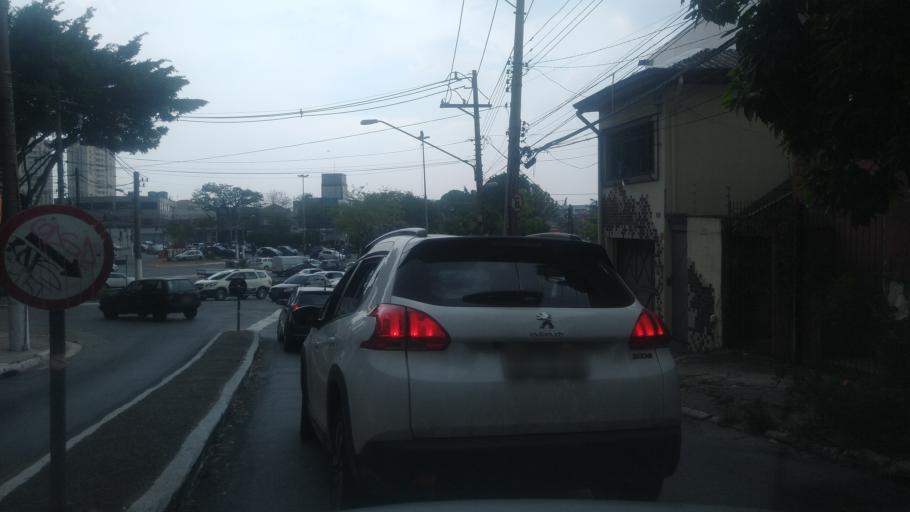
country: BR
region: Sao Paulo
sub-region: Sao Paulo
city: Sao Paulo
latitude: -23.4999
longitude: -46.6151
